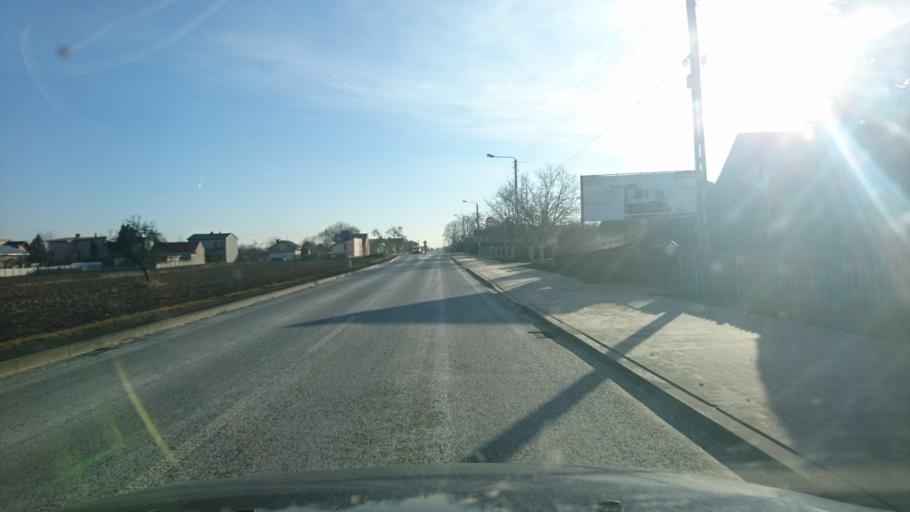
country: PL
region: Silesian Voivodeship
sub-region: Powiat klobucki
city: Starokrzepice
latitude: 51.0185
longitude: 18.6527
